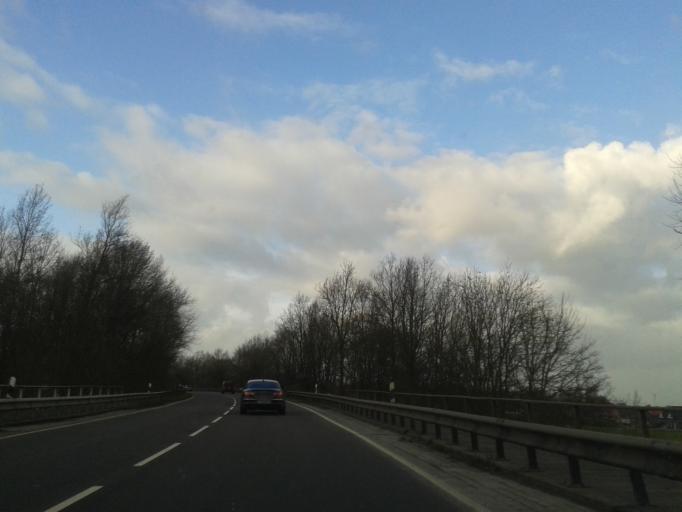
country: DE
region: Lower Saxony
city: Upgant-Schott
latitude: 53.5224
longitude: 7.2806
